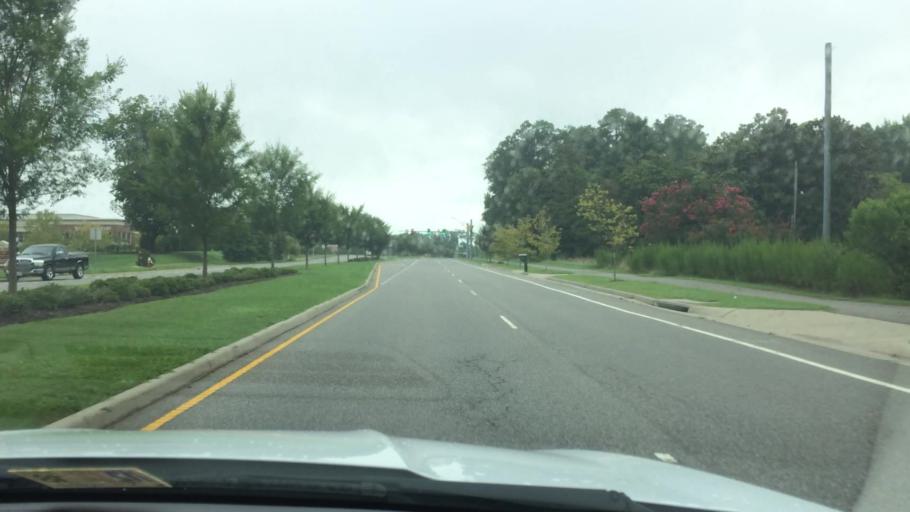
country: US
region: Virginia
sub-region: James City County
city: Williamsburg
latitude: 37.2779
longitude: -76.7380
